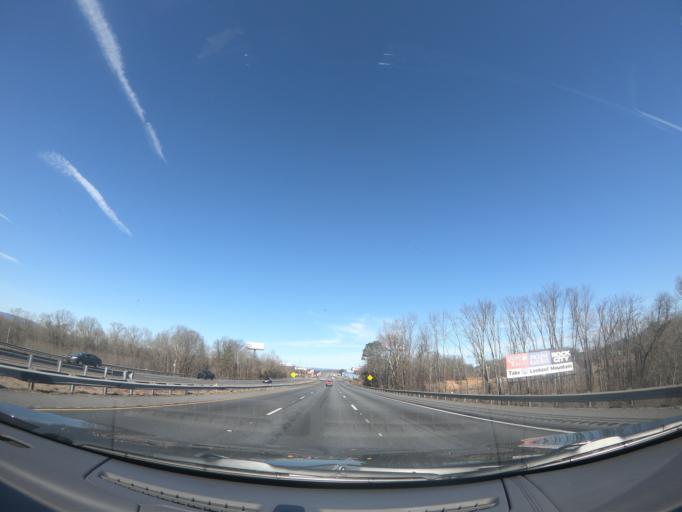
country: US
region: Georgia
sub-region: Catoosa County
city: Indian Springs
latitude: 34.9779
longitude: -85.1977
